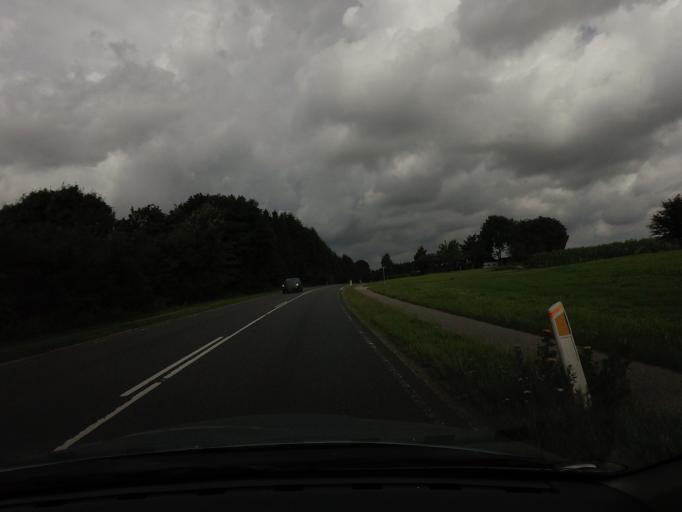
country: DK
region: North Denmark
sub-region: Hjorring Kommune
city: Tars
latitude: 57.4120
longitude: 10.0643
